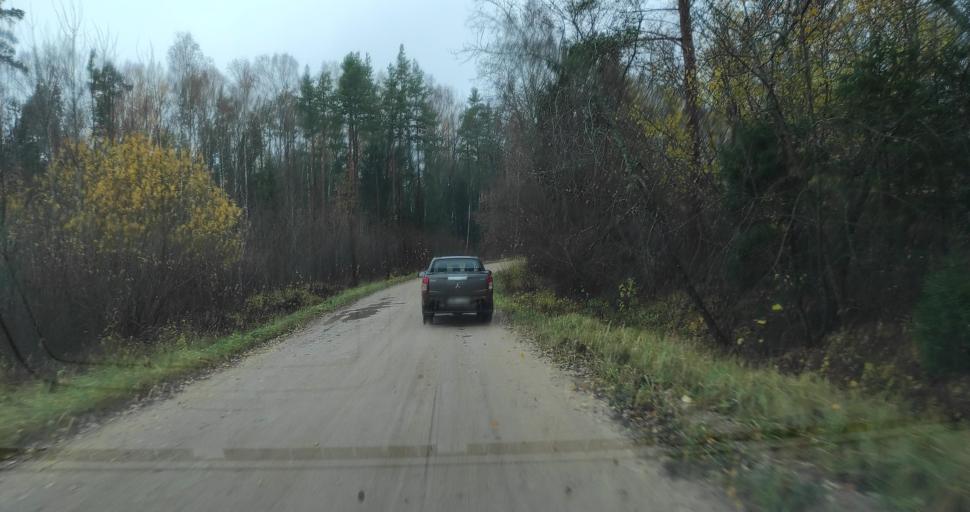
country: LV
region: Skrunda
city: Skrunda
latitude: 56.6868
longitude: 22.0760
